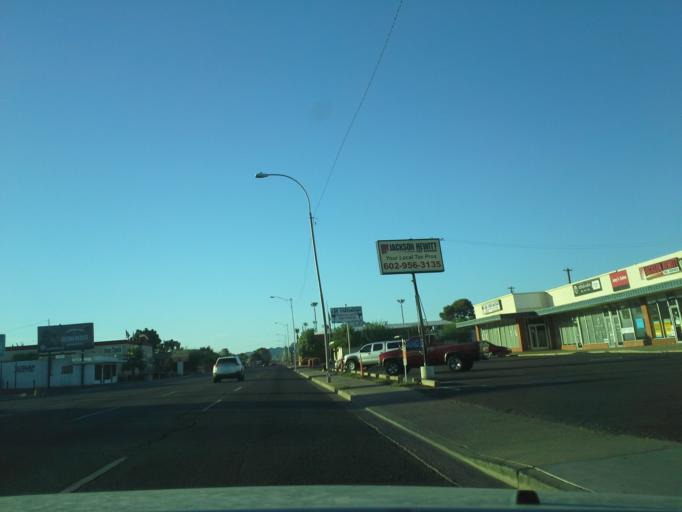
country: US
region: Arizona
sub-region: Maricopa County
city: Phoenix
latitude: 33.4830
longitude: -112.0301
